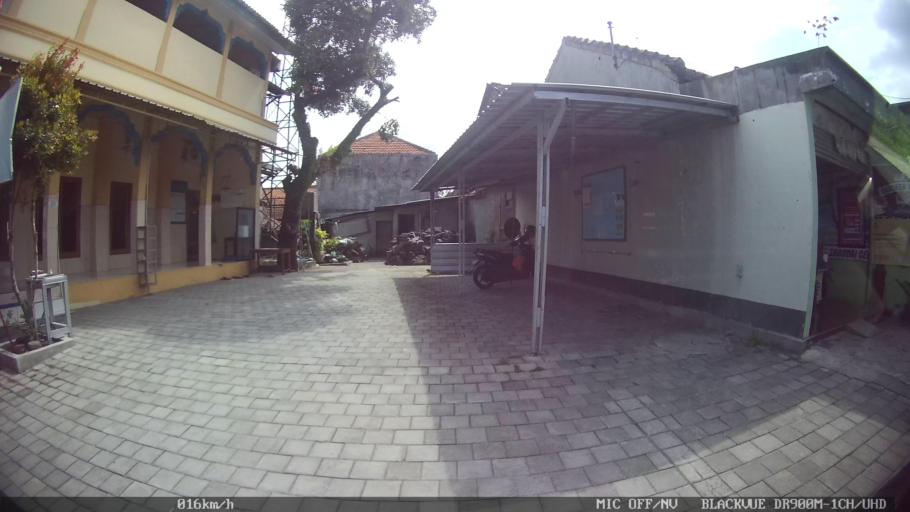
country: ID
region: Daerah Istimewa Yogyakarta
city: Depok
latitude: -7.7725
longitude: 110.4377
